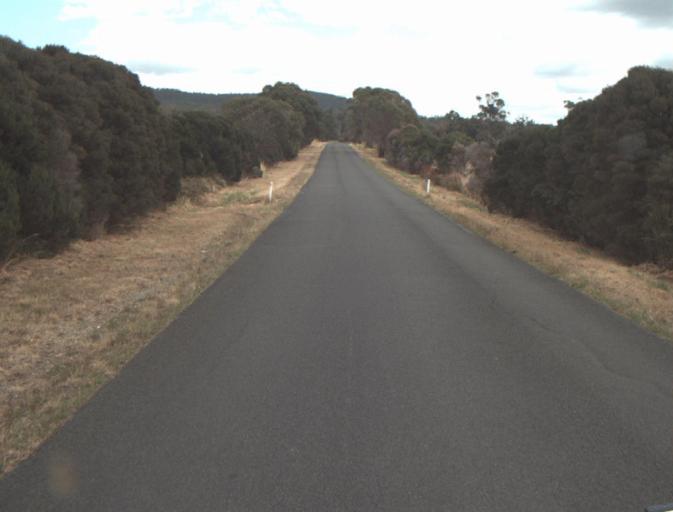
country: AU
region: Tasmania
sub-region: Launceston
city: Mayfield
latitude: -41.2070
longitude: 147.0612
